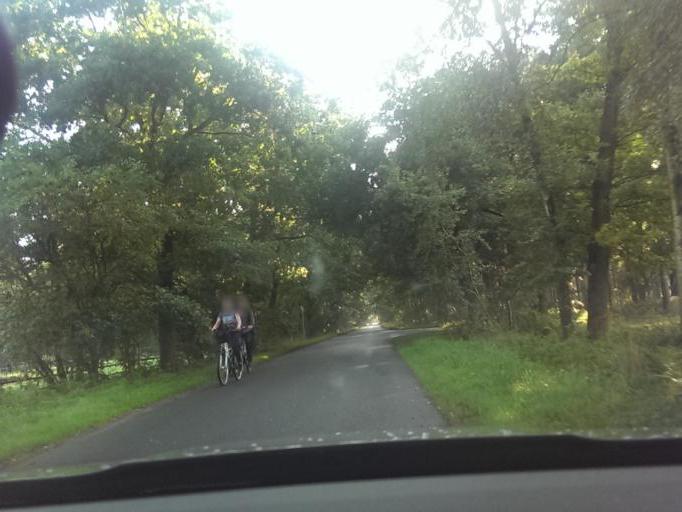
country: DE
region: Lower Saxony
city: Elze
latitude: 52.5636
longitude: 9.7913
